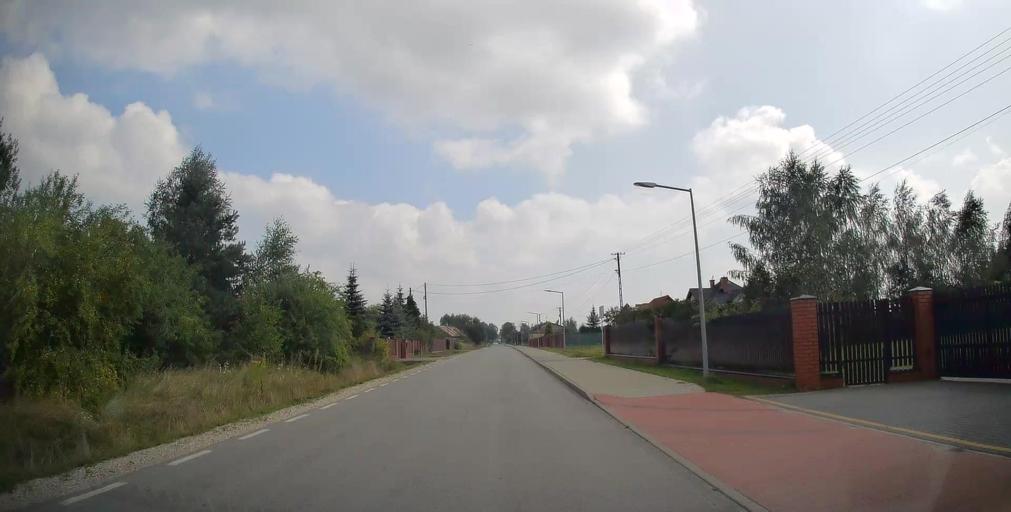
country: PL
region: Masovian Voivodeship
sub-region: Powiat bialobrzeski
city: Sucha
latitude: 51.6106
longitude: 20.9731
